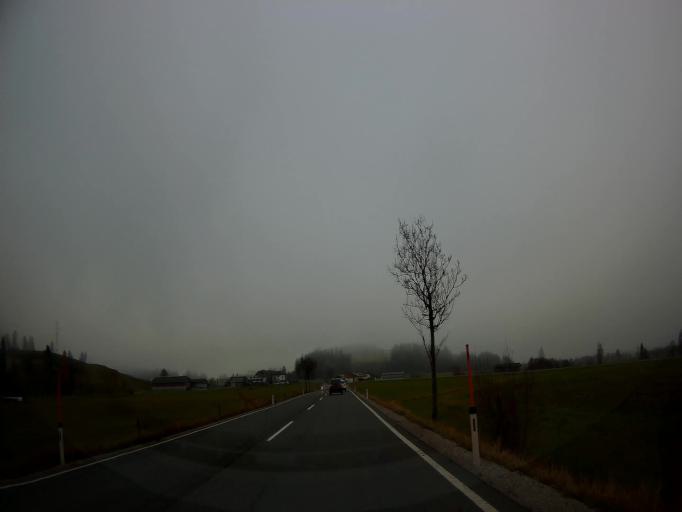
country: AT
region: Salzburg
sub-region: Politischer Bezirk Zell am See
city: Saalfelden am Steinernen Meer
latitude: 47.4588
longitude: 12.8293
